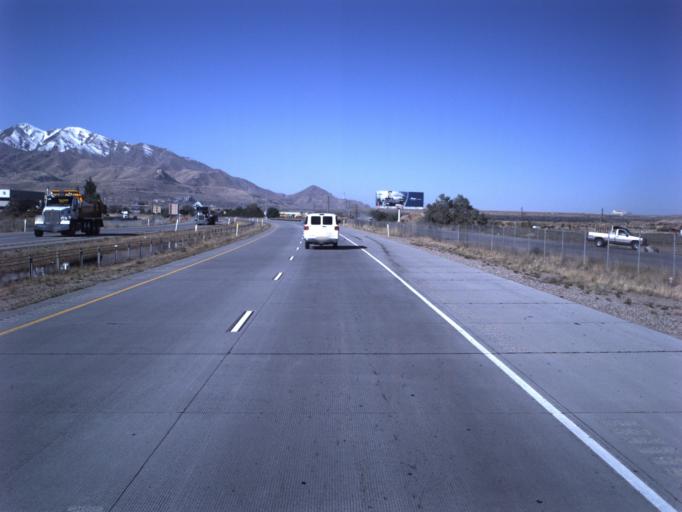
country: US
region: Utah
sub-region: Salt Lake County
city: West Valley City
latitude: 40.7258
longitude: -112.0339
